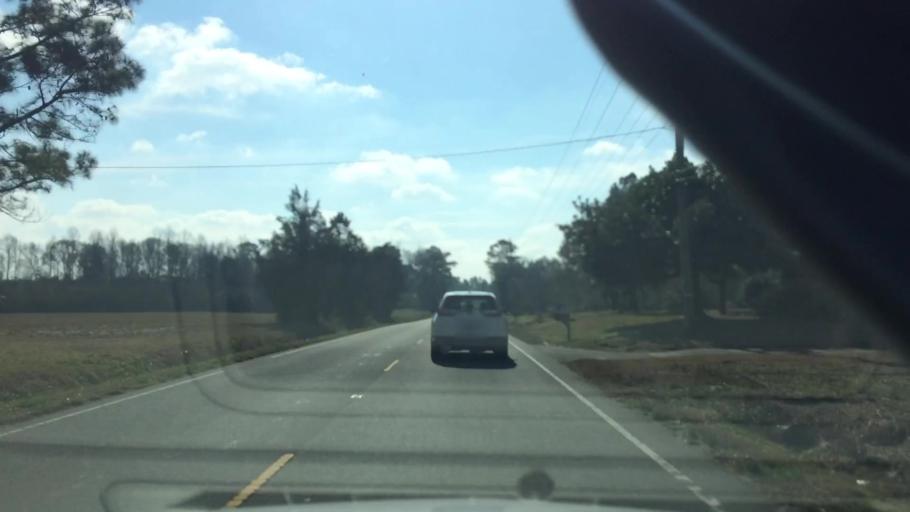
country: US
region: North Carolina
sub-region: Duplin County
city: Beulaville
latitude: 34.8937
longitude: -77.7825
